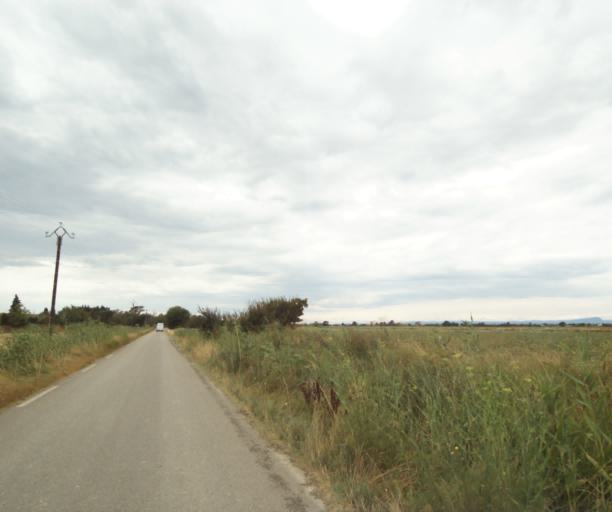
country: FR
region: Languedoc-Roussillon
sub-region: Departement de l'Herault
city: La Grande-Motte
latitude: 43.5963
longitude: 4.1144
